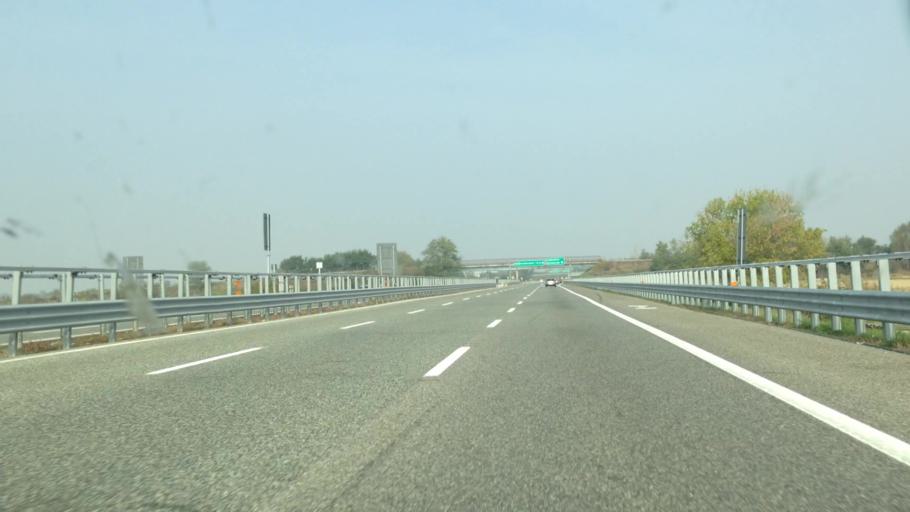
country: IT
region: Piedmont
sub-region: Provincia di Vercelli
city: Stroppiana
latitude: 45.2363
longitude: 8.4714
